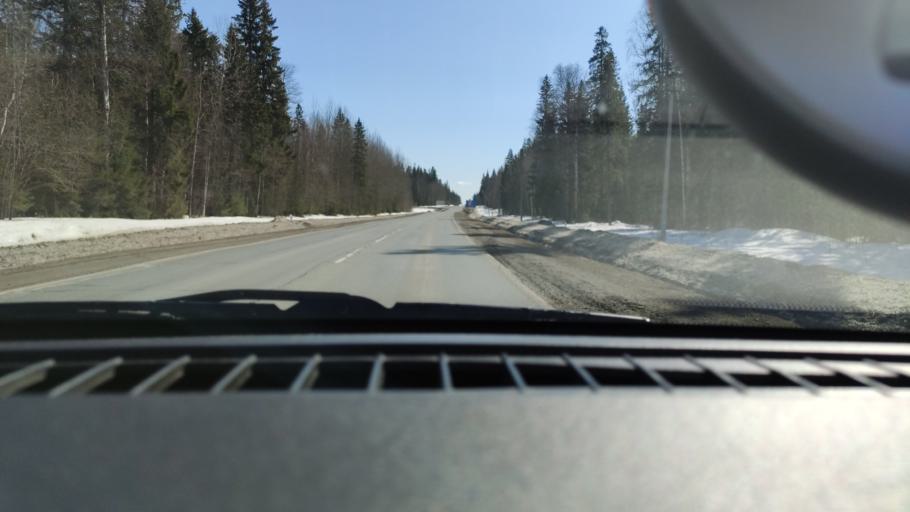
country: RU
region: Perm
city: Perm
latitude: 58.2005
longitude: 56.2056
